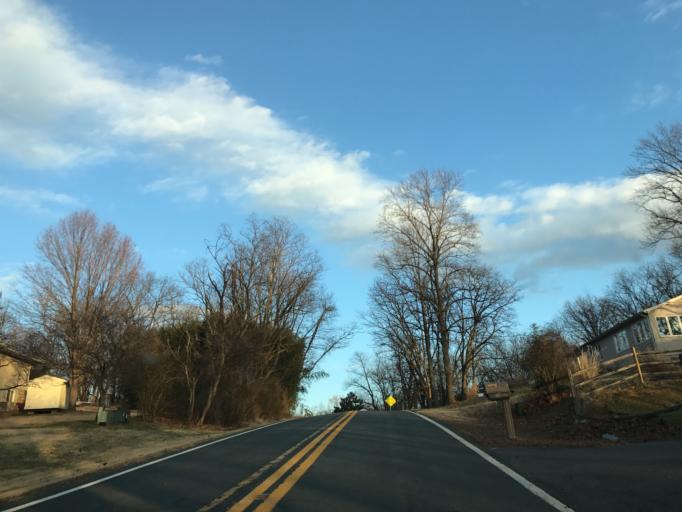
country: US
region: Maryland
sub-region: Cecil County
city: Charlestown
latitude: 39.4624
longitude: -76.0008
